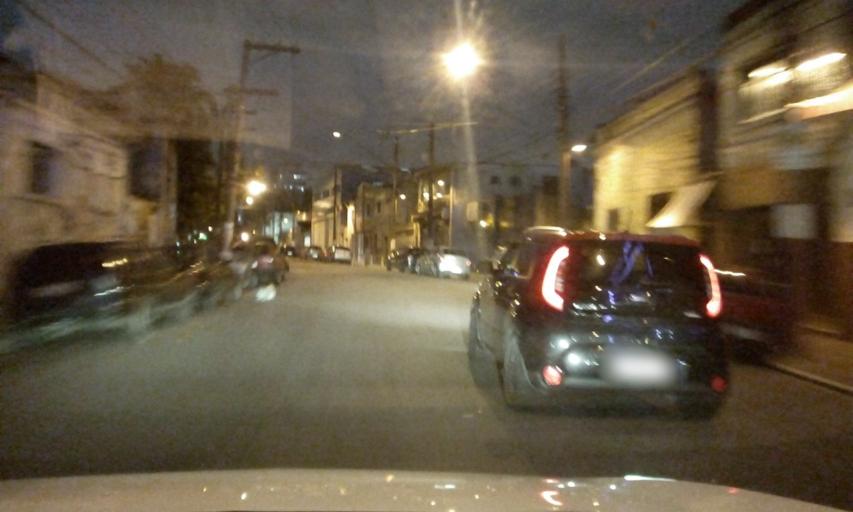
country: BR
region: Sao Paulo
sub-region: Sao Paulo
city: Sao Paulo
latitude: -23.5440
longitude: -46.5830
